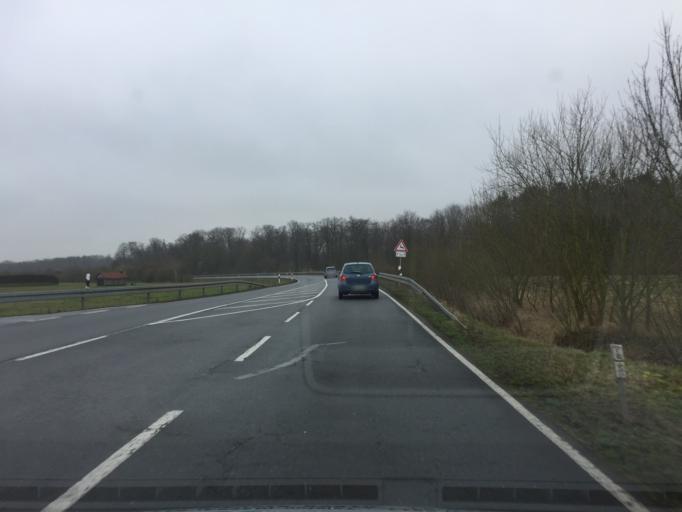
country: DE
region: Lower Saxony
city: Wiedensahl
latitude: 52.3715
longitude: 9.1145
